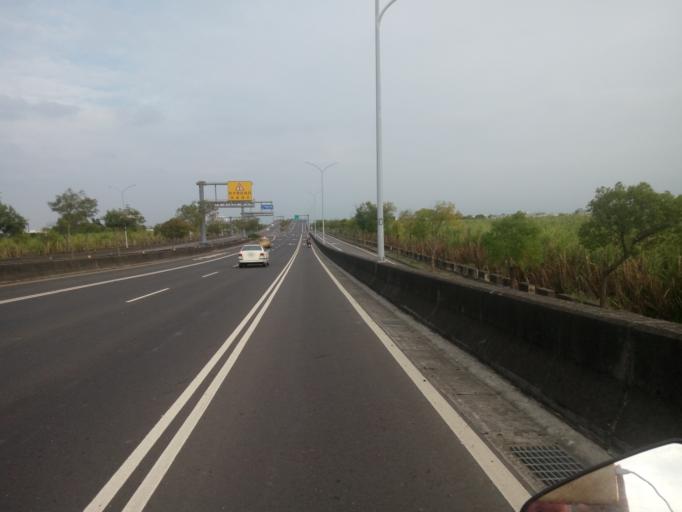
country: TW
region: Taiwan
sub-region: Chiayi
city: Taibao
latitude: 23.4852
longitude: 120.3789
